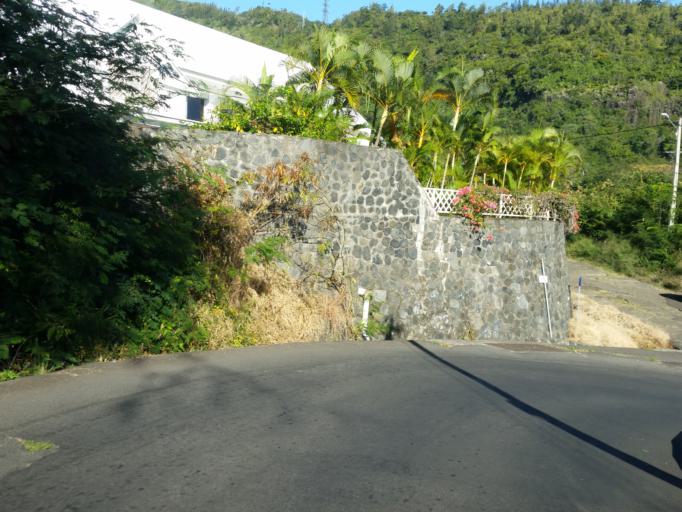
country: RE
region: Reunion
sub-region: Reunion
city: Saint-Denis
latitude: -20.9019
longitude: 55.4561
